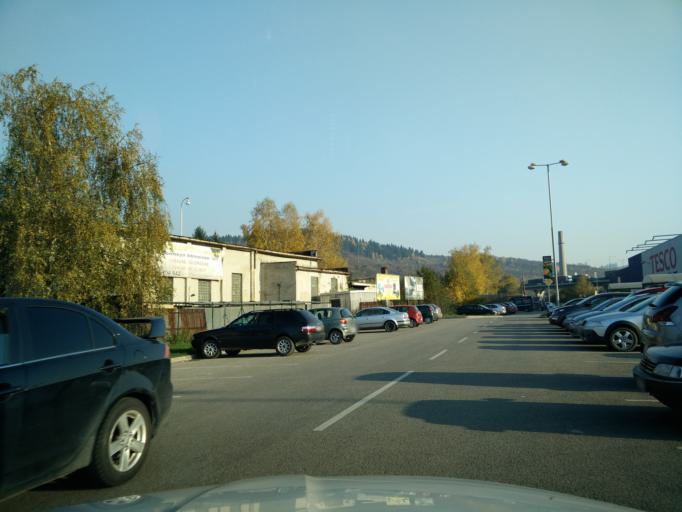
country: SK
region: Zilinsky
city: Cadca
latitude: 49.4415
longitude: 18.7907
